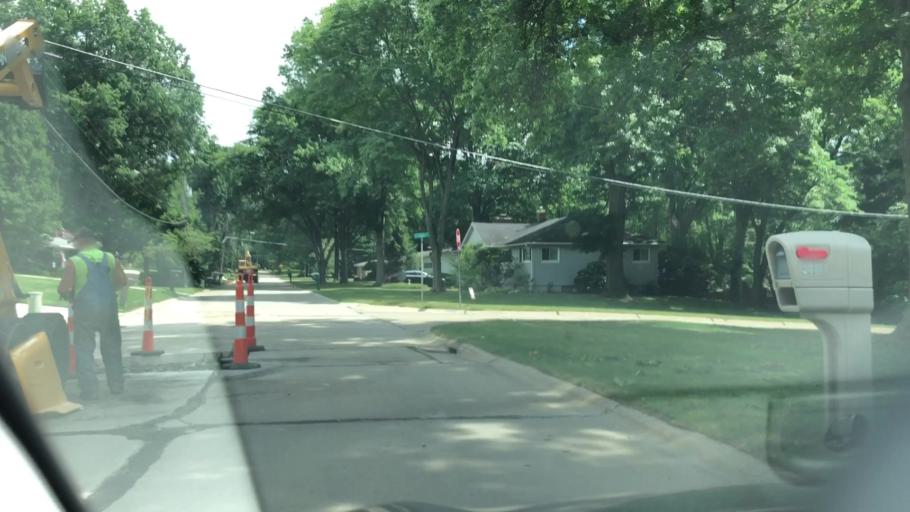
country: US
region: Ohio
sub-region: Summit County
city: Fairlawn
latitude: 41.1274
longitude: -81.6234
